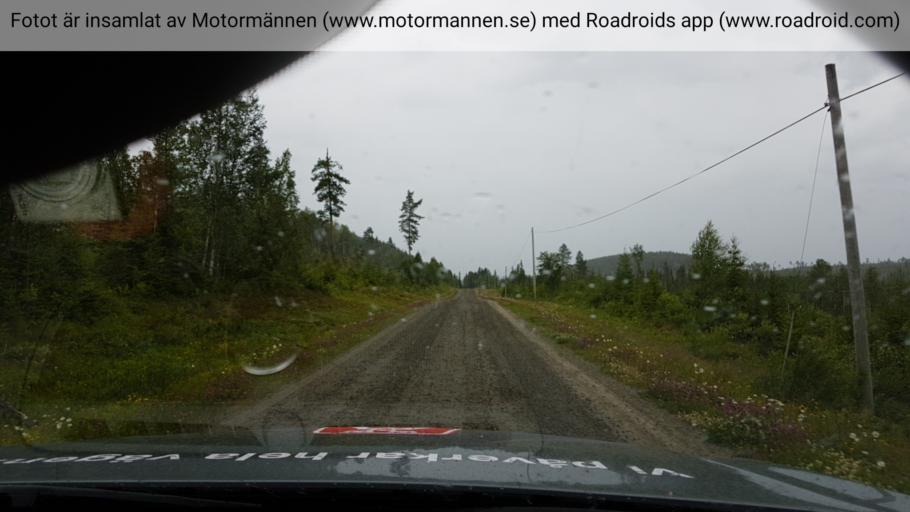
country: SE
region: Jaemtland
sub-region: Bergs Kommun
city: Hoverberg
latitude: 62.5361
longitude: 14.7022
